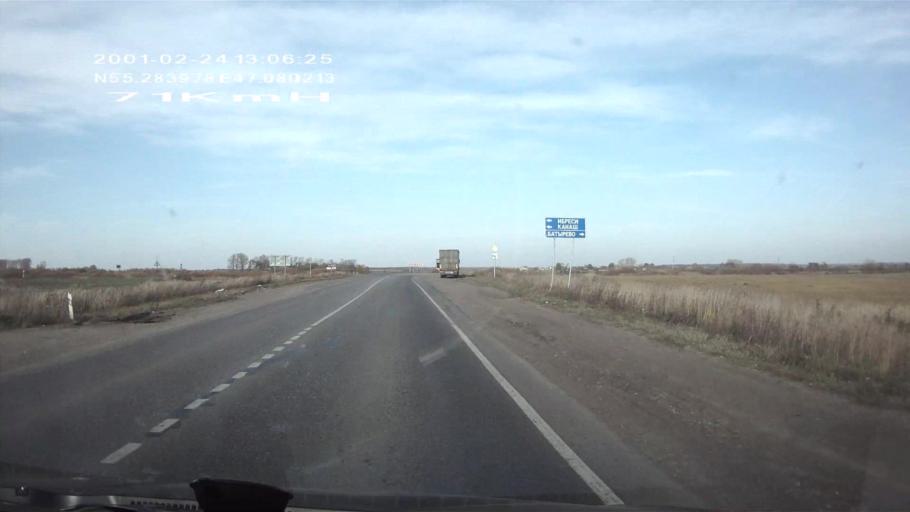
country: RU
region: Chuvashia
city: Ibresi
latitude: 55.2840
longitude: 47.0802
